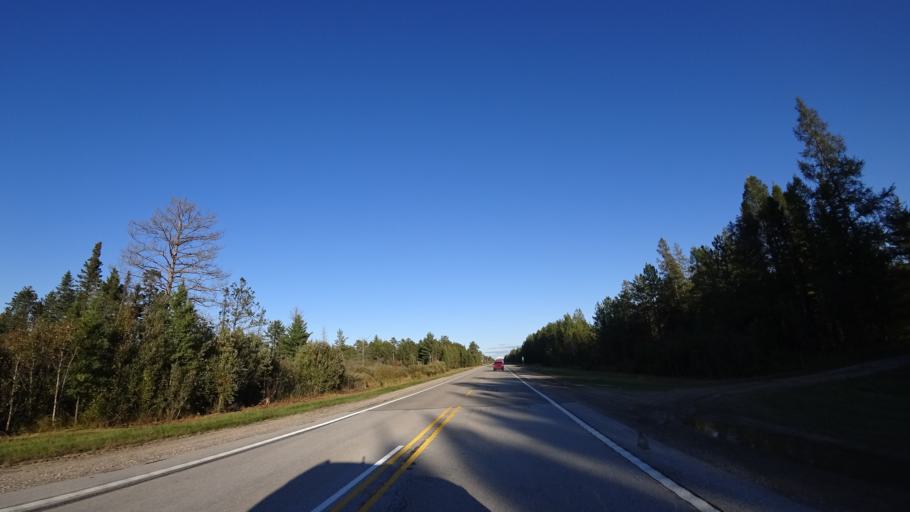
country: US
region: Michigan
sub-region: Schoolcraft County
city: Manistique
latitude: 46.3454
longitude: -86.0881
